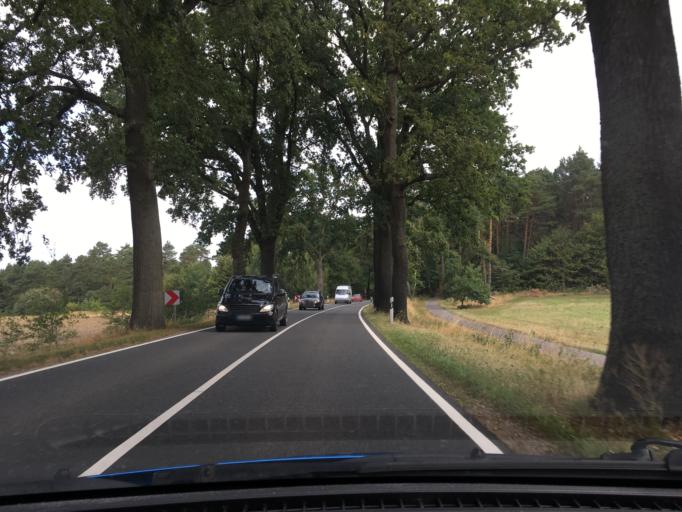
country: DE
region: Mecklenburg-Vorpommern
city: Malliss
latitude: 53.2035
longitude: 11.3034
